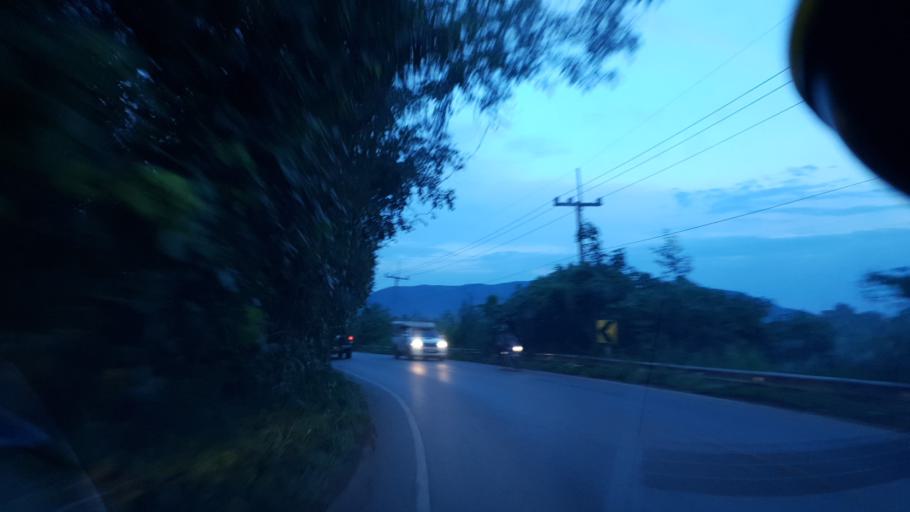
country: TH
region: Chiang Rai
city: Wiang Chiang Rung
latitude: 19.9654
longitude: 99.9845
